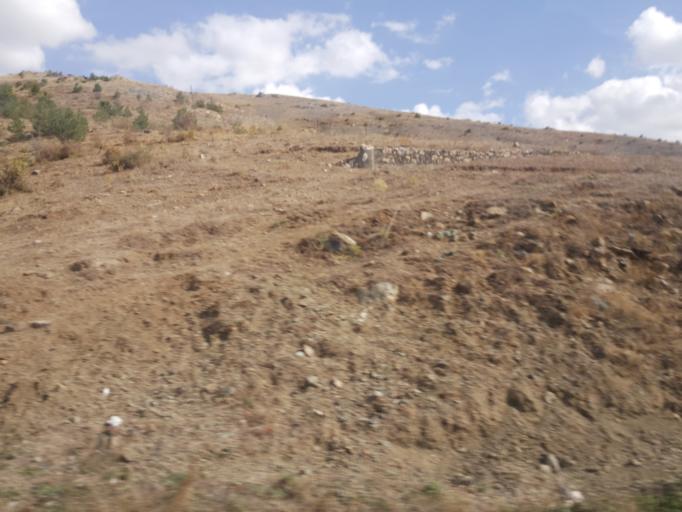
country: TR
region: Tokat
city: Artova
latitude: 40.0973
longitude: 36.3021
